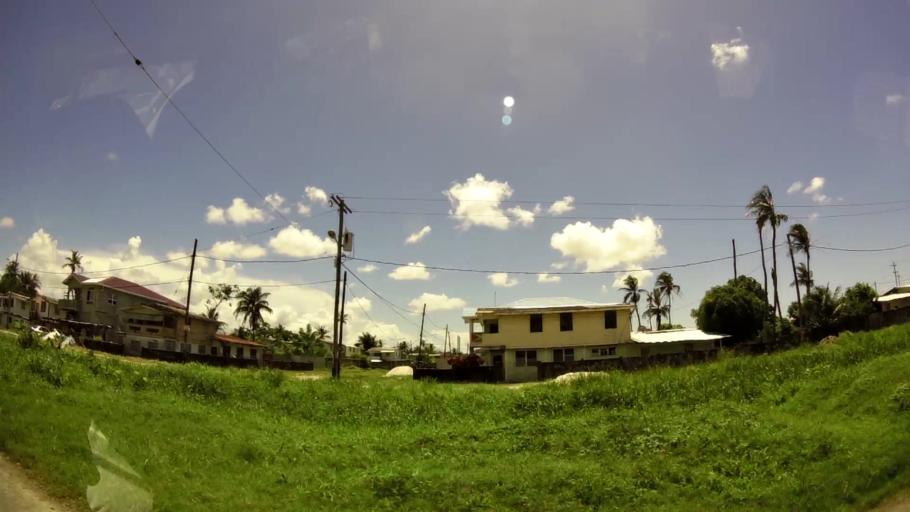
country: GY
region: Demerara-Mahaica
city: Georgetown
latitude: 6.7882
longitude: -58.1508
